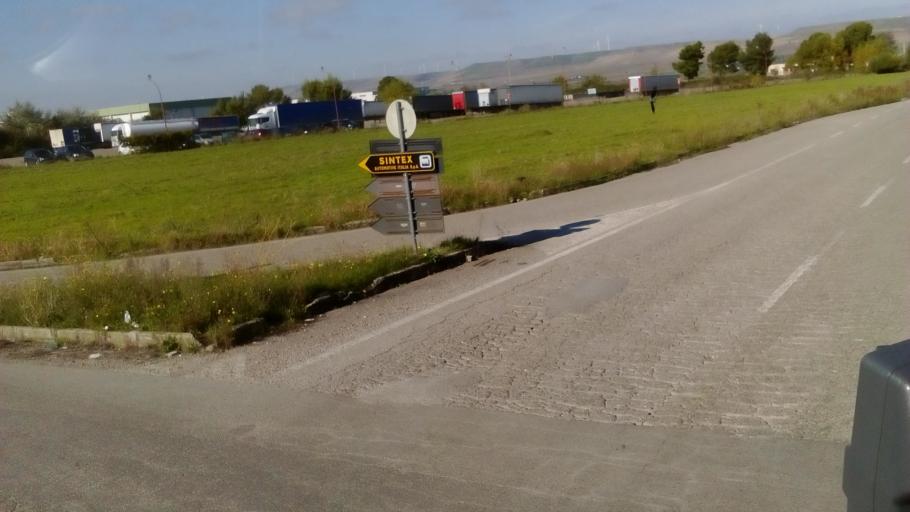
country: IT
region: Basilicate
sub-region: Provincia di Potenza
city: Melfi
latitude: 41.0759
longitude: 15.6920
